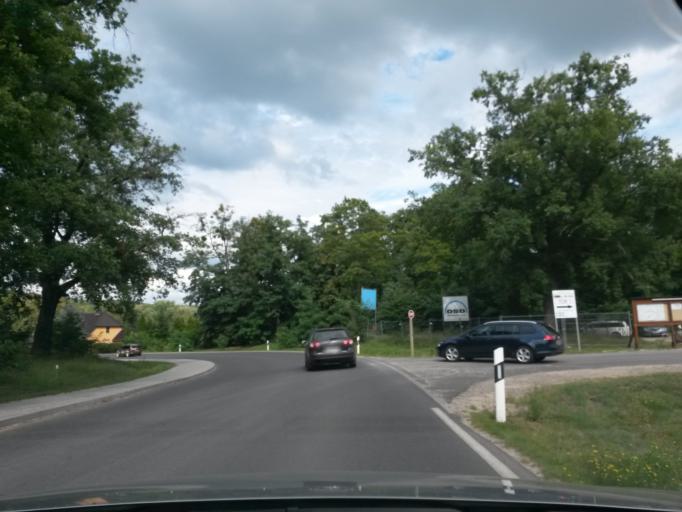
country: DE
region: Brandenburg
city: Niederfinow
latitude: 52.8518
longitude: 13.9442
